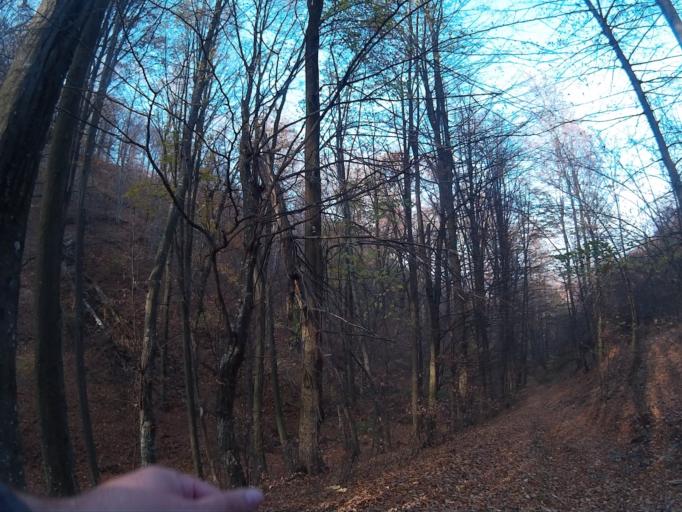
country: HU
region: Heves
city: Belapatfalva
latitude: 48.0613
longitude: 20.4032
